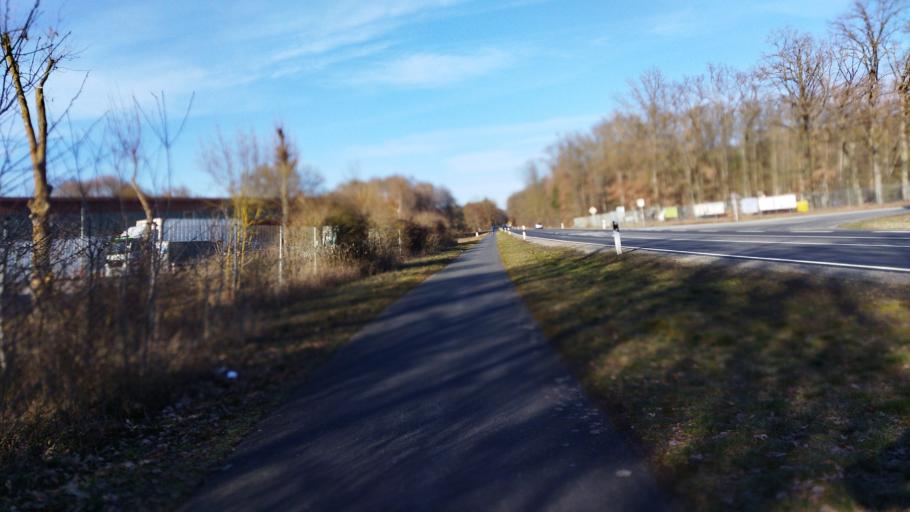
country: DE
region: Bavaria
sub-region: Regierungsbezirk Unterfranken
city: Sennfeld
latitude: 50.0275
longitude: 10.2415
